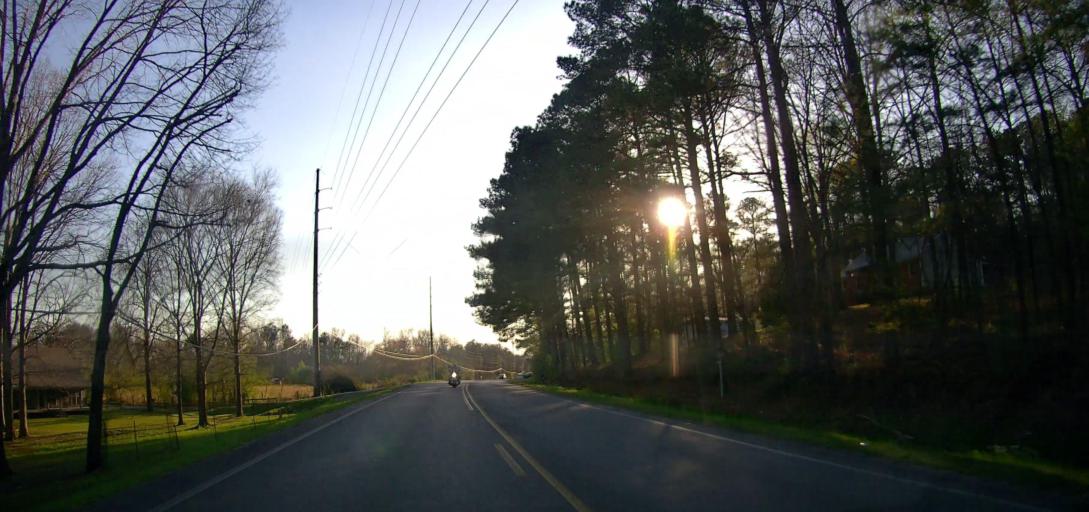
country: US
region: Alabama
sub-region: Shelby County
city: Indian Springs Village
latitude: 33.3282
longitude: -86.6957
